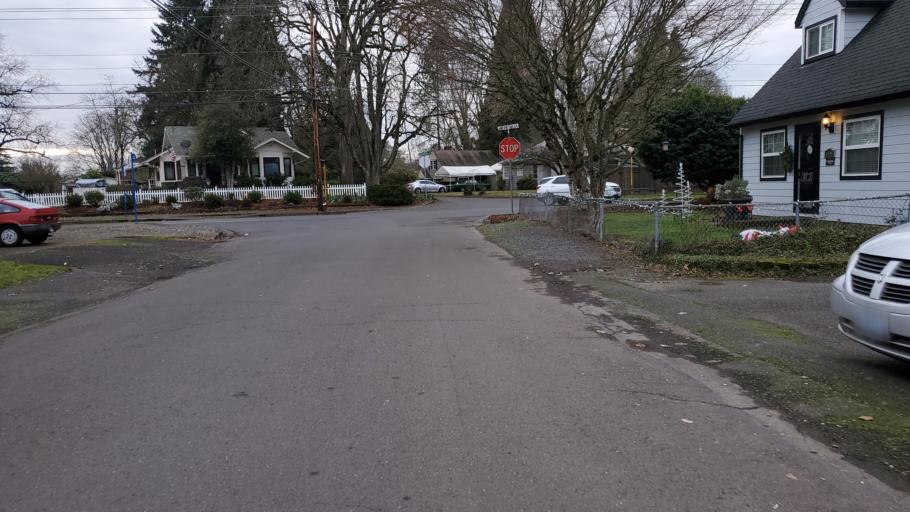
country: US
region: Oregon
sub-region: Clackamas County
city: Gladstone
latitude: 45.3844
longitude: -122.6013
